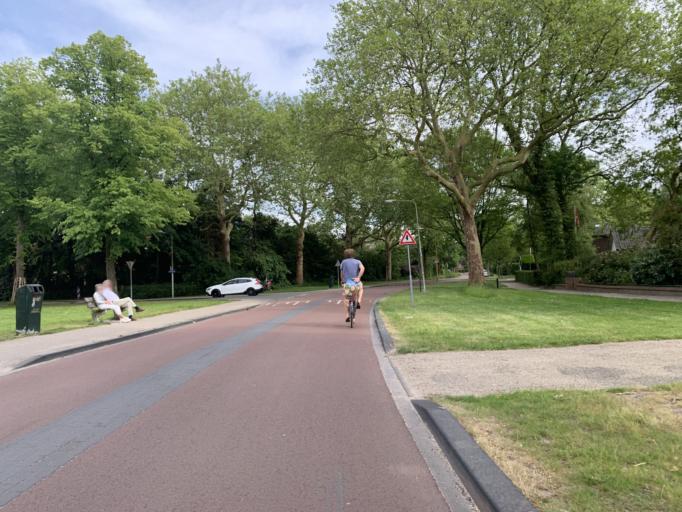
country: NL
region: Groningen
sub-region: Gemeente Haren
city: Haren
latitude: 53.1732
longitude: 6.6099
